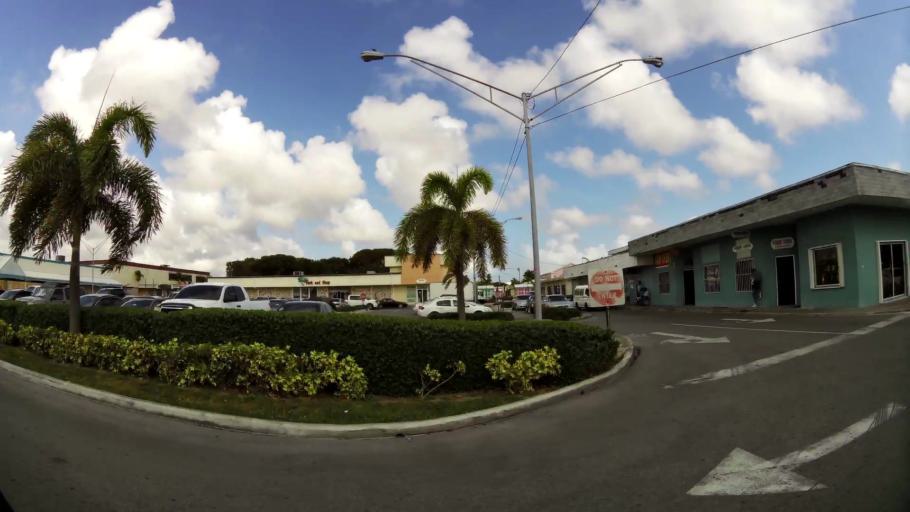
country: BS
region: Freeport
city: Freeport
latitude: 26.5312
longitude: -78.6964
